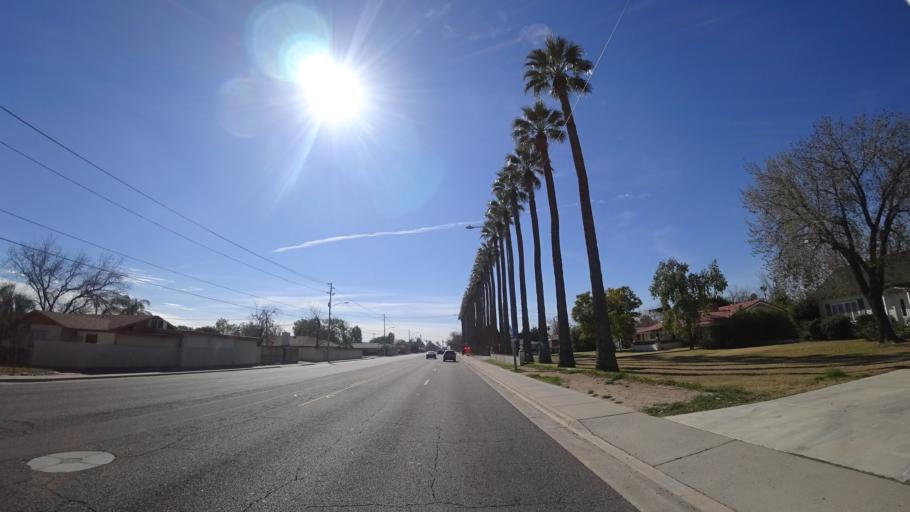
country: US
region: Arizona
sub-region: Maricopa County
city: Glendale
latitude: 33.5477
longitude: -112.1863
